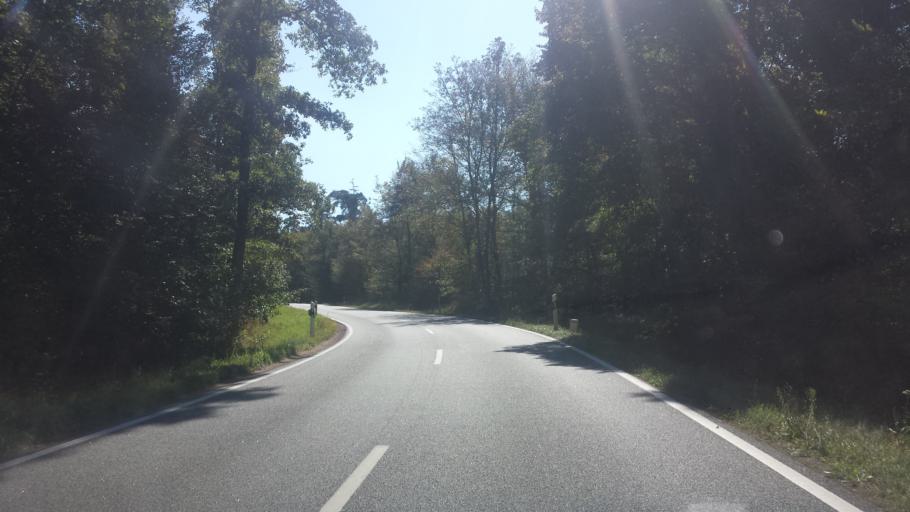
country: DE
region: Hesse
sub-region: Regierungsbezirk Darmstadt
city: Einhausen
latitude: 49.7063
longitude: 8.5393
